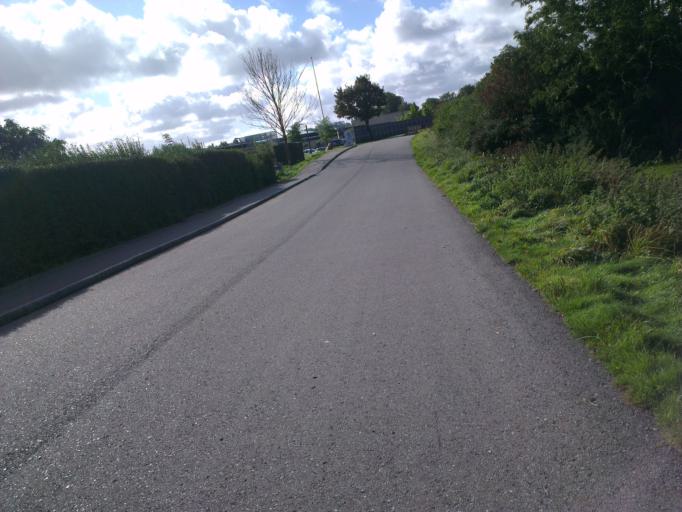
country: DK
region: Capital Region
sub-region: Frederikssund Kommune
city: Slangerup
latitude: 55.8447
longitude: 12.1644
